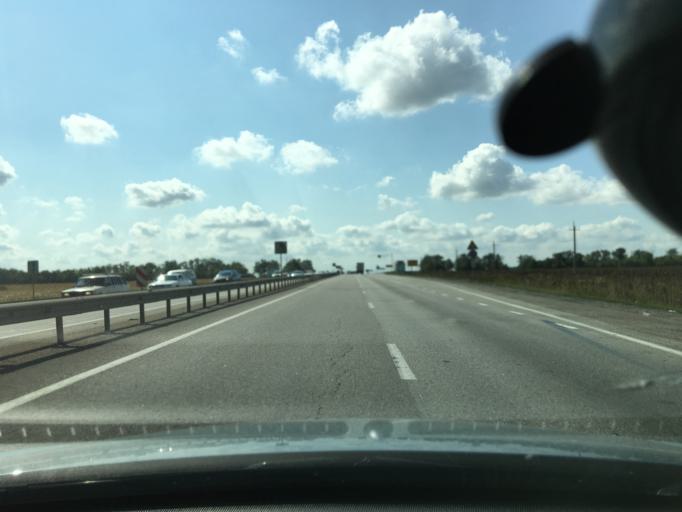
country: RU
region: Krasnodarskiy
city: Krasnoye
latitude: 46.7568
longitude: 39.6606
